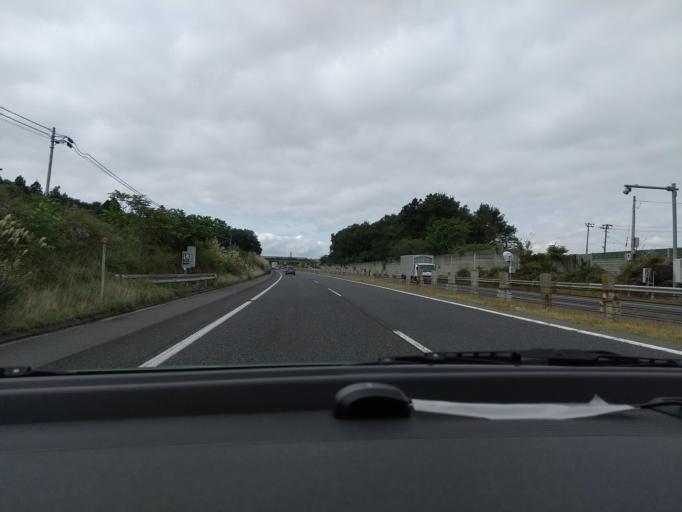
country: JP
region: Iwate
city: Kitakami
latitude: 39.2102
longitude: 141.1037
